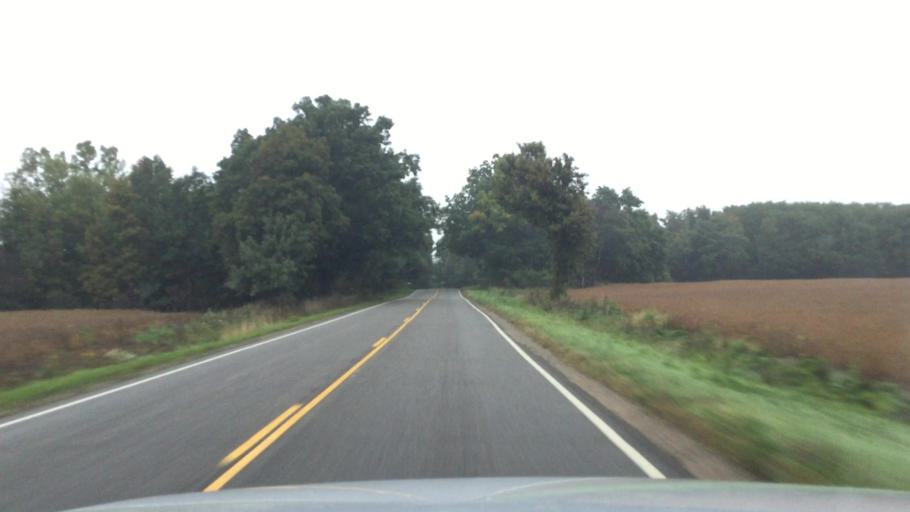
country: US
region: Michigan
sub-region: Shiawassee County
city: Corunna
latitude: 42.9299
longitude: -84.1243
